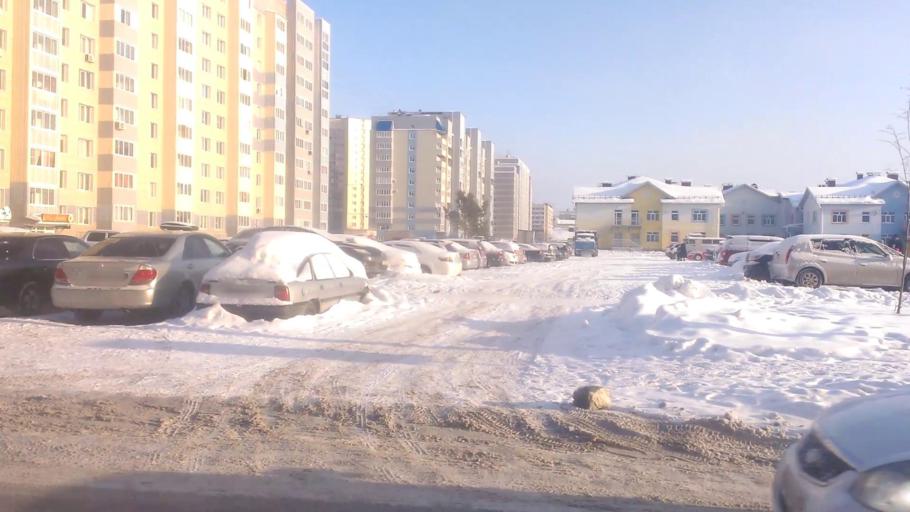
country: RU
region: Altai Krai
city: Novosilikatnyy
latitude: 53.3438
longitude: 83.6556
